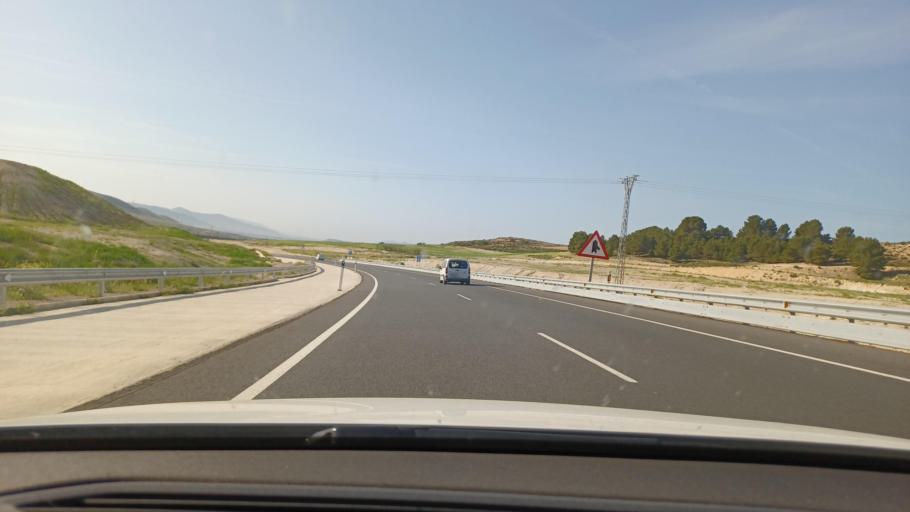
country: ES
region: Castille-La Mancha
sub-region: Provincia de Albacete
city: Caudete
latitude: 38.7240
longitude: -0.9380
